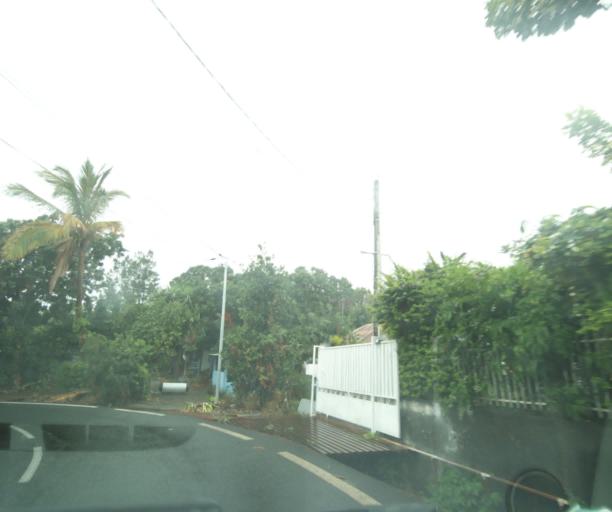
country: RE
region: Reunion
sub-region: Reunion
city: Saint-Paul
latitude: -21.0245
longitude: 55.2865
